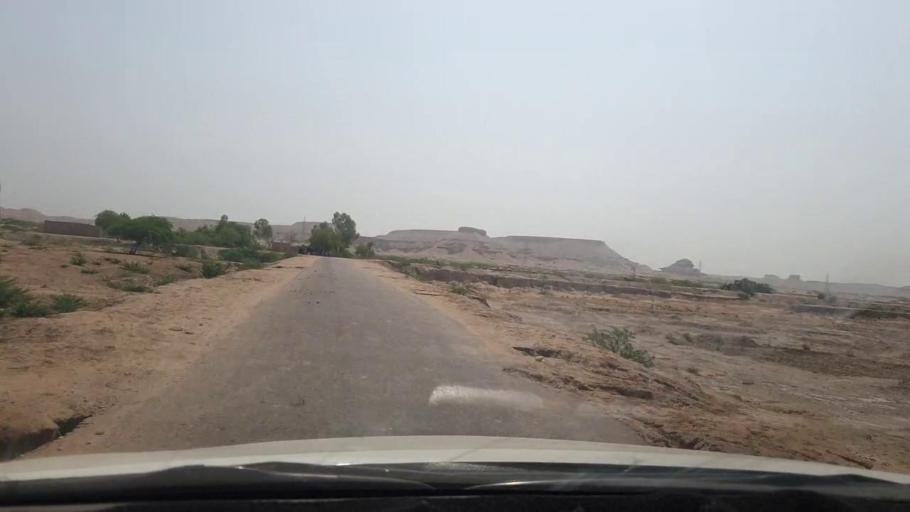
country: PK
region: Sindh
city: Rohri
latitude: 27.6061
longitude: 68.9143
